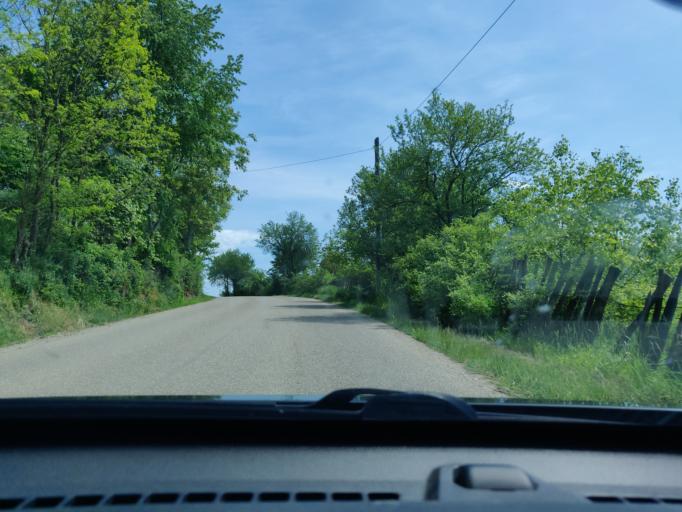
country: RO
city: Vizantea-Manastireasca
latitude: 45.9947
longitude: 26.7790
